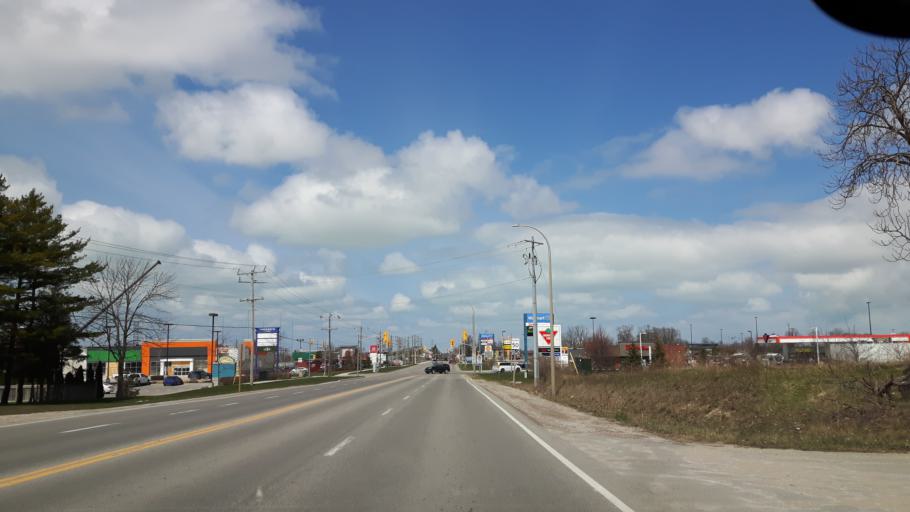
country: CA
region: Ontario
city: Goderich
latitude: 43.7288
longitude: -81.6872
